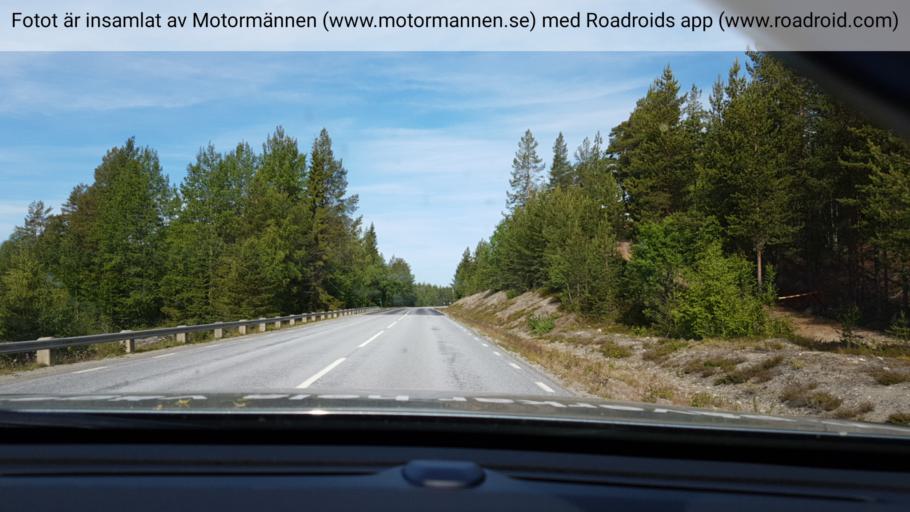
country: SE
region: Vaesterbotten
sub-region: Asele Kommun
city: Asele
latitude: 64.1891
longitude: 17.1141
